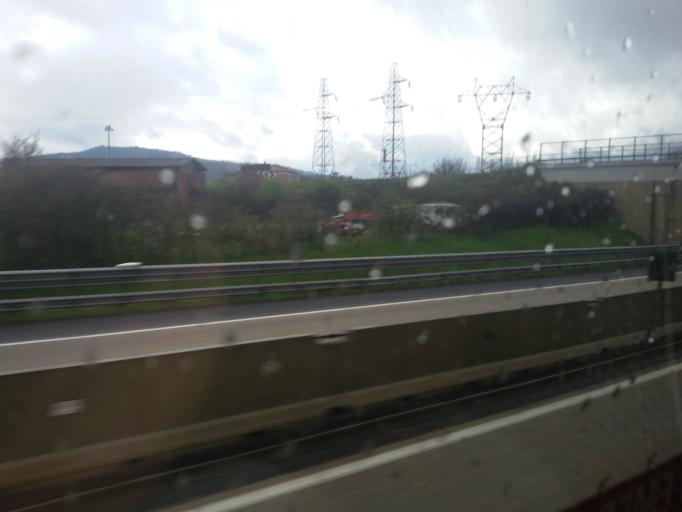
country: IT
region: Tuscany
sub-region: Province of Arezzo
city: Ponticino
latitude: 43.4841
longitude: 11.7190
